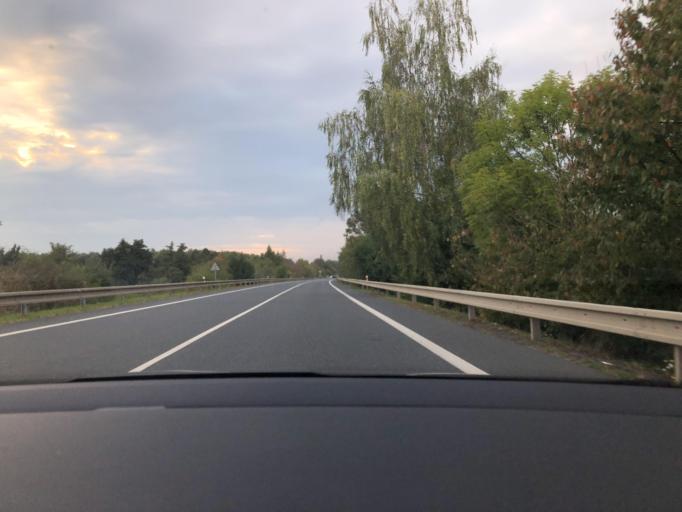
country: CZ
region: Central Bohemia
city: Planany
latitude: 50.0446
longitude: 15.0253
